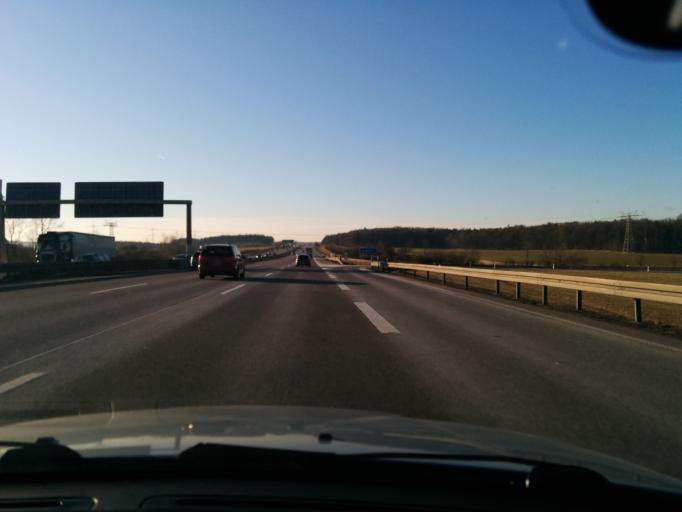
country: DE
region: Thuringia
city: Hetschburg
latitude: 50.9444
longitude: 11.2968
